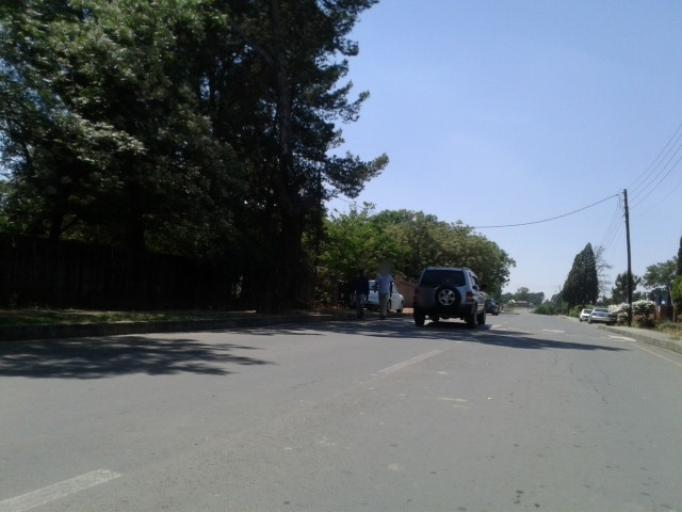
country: LS
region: Maseru
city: Maseru
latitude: -29.3056
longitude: 27.4699
